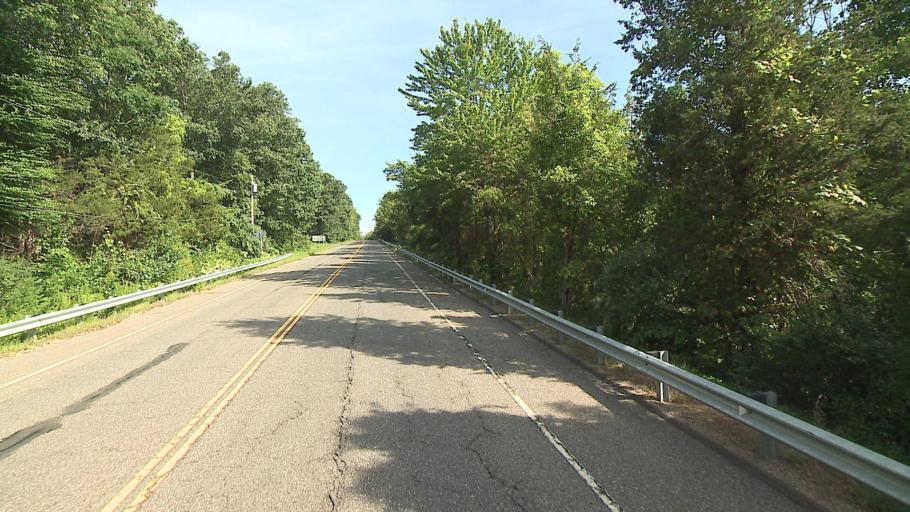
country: US
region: Connecticut
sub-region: Litchfield County
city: Thomaston
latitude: 41.6782
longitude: -73.0916
